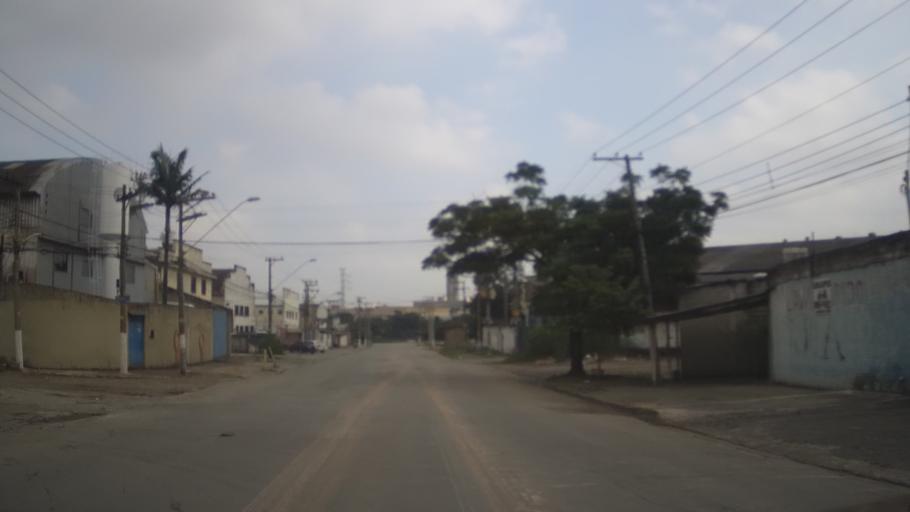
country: BR
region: Sao Paulo
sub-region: Guarulhos
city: Guarulhos
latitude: -23.4656
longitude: -46.4701
